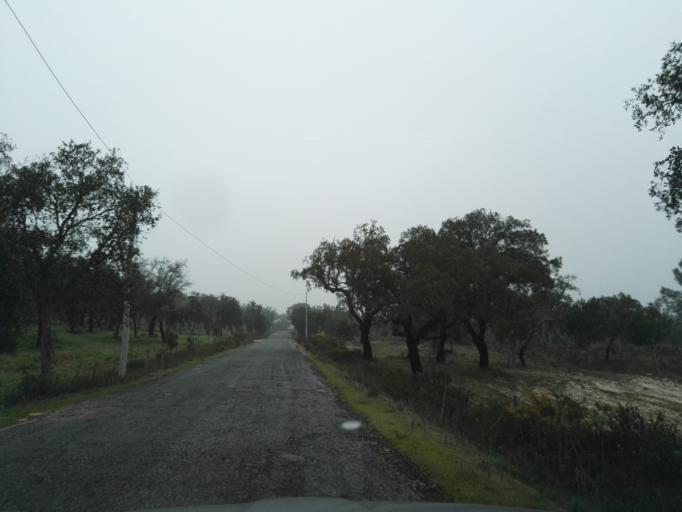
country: PT
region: Evora
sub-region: Vendas Novas
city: Vendas Novas
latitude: 38.7978
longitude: -8.3363
